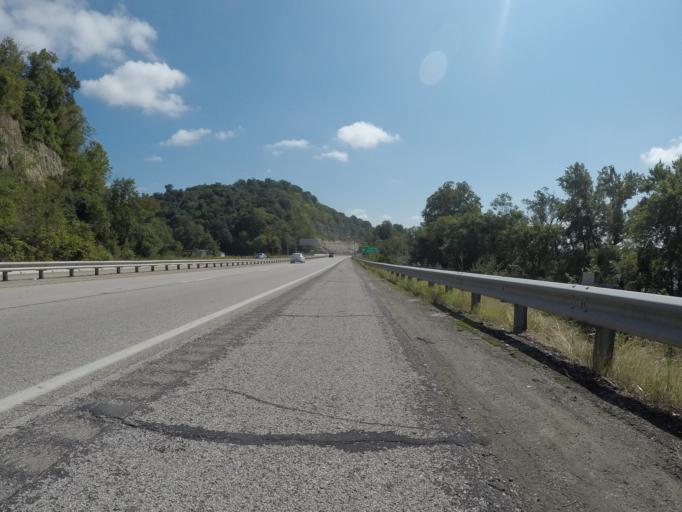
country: US
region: Kentucky
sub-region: Boyd County
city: Ashland
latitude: 38.4813
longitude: -82.6252
